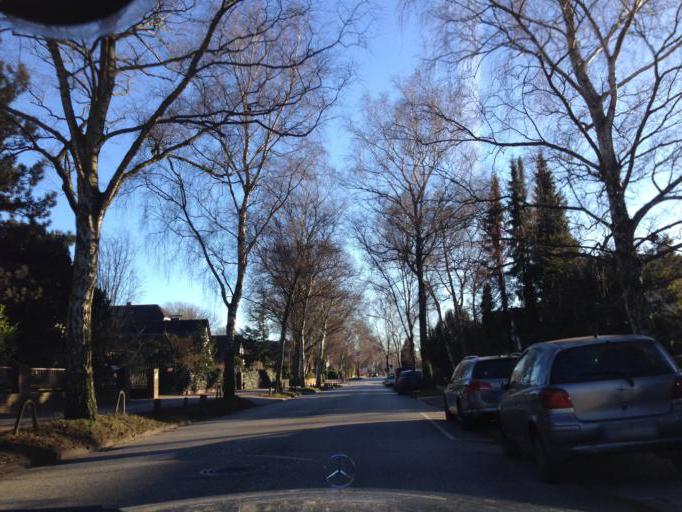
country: DE
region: Hamburg
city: Farmsen-Berne
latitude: 53.6185
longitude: 10.1351
